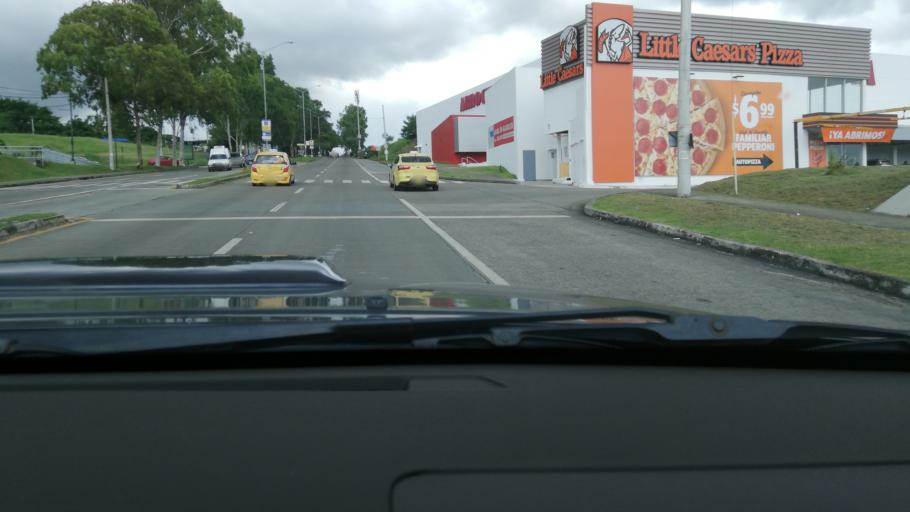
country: PA
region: Panama
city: San Miguelito
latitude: 9.0399
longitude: -79.4794
